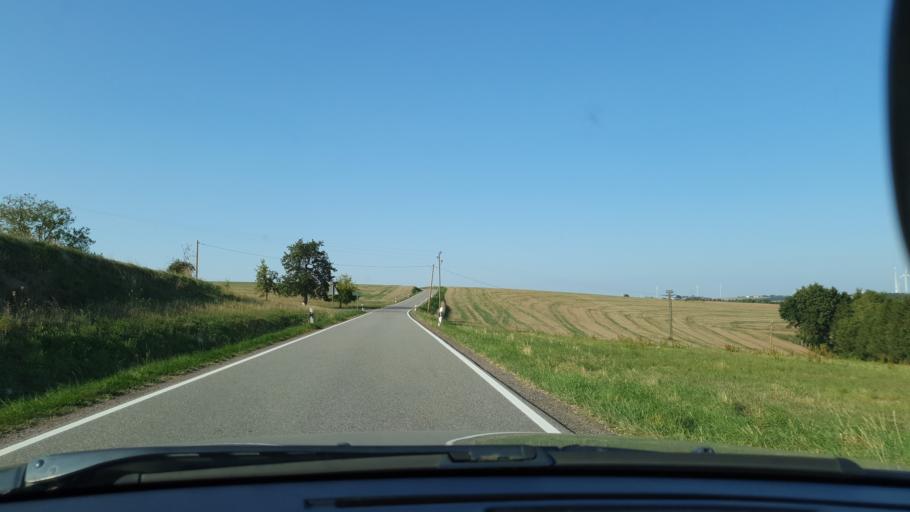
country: DE
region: Rheinland-Pfalz
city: Herschberg
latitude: 49.2898
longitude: 7.5608
